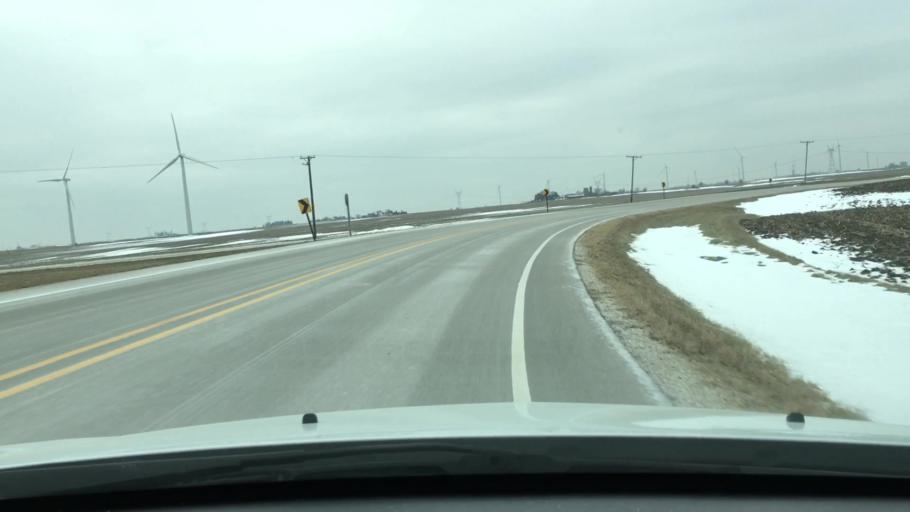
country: US
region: Illinois
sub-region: DeKalb County
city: Waterman
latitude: 41.7906
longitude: -88.8864
